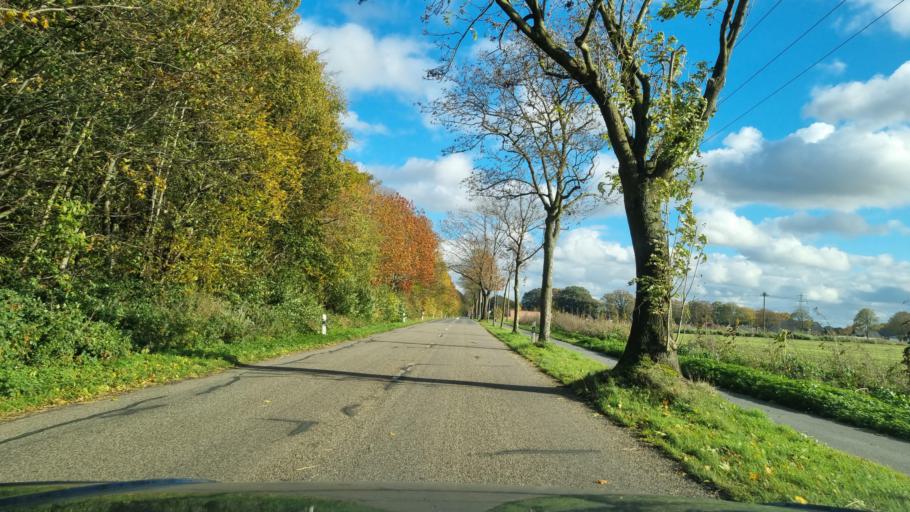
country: DE
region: North Rhine-Westphalia
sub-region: Regierungsbezirk Dusseldorf
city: Kleve
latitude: 51.7670
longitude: 6.1599
